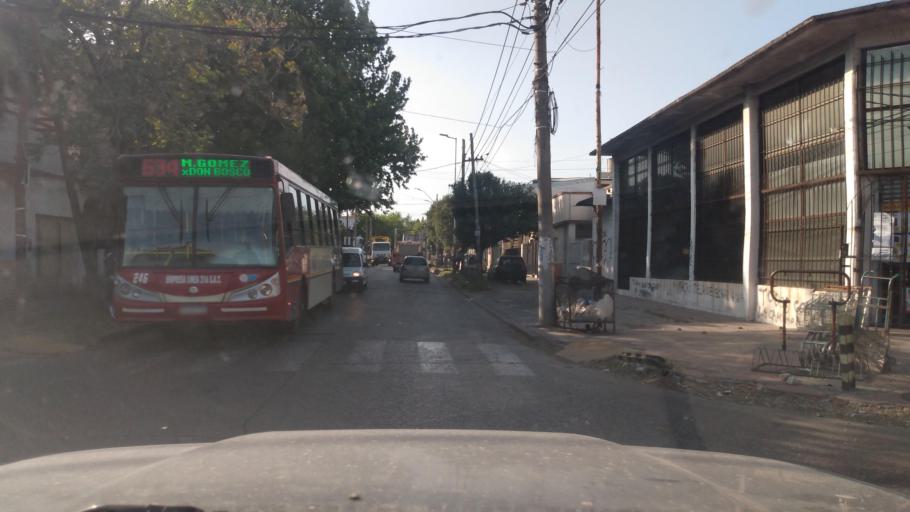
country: AR
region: Buenos Aires
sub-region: Partido de Moron
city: Moron
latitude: -34.6390
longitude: -58.6186
